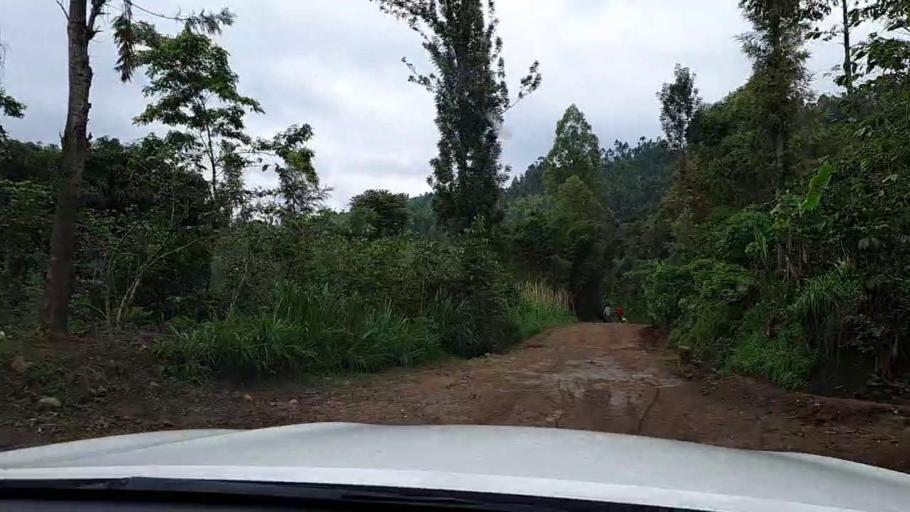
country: RW
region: Western Province
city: Cyangugu
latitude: -2.5514
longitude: 29.0373
